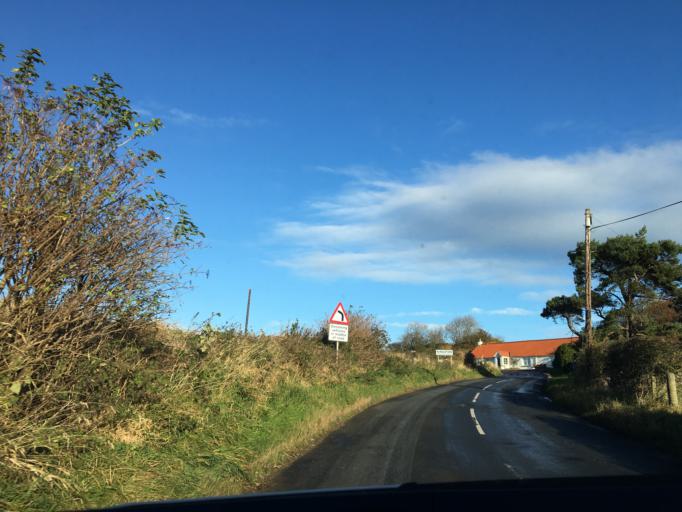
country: GB
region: Scotland
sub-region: East Lothian
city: North Berwick
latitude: 56.0301
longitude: -2.7364
